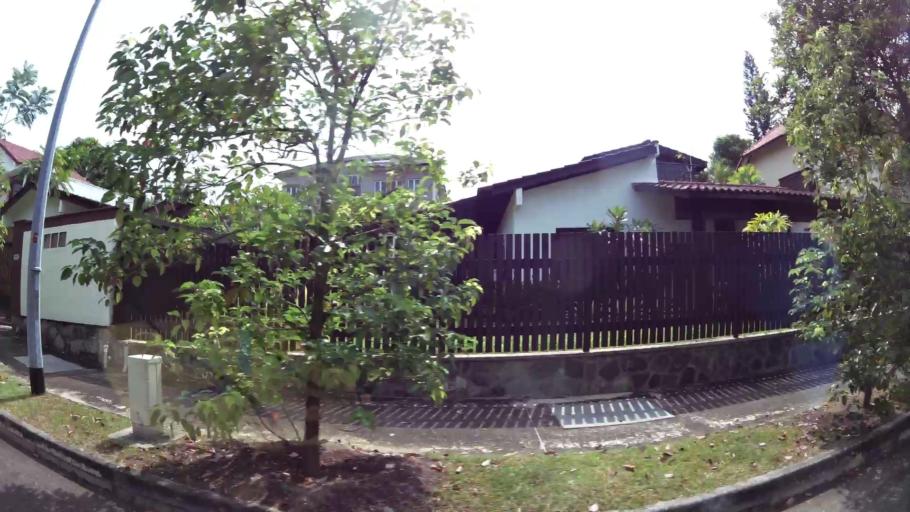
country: SG
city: Singapore
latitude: 1.3267
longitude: 103.7671
